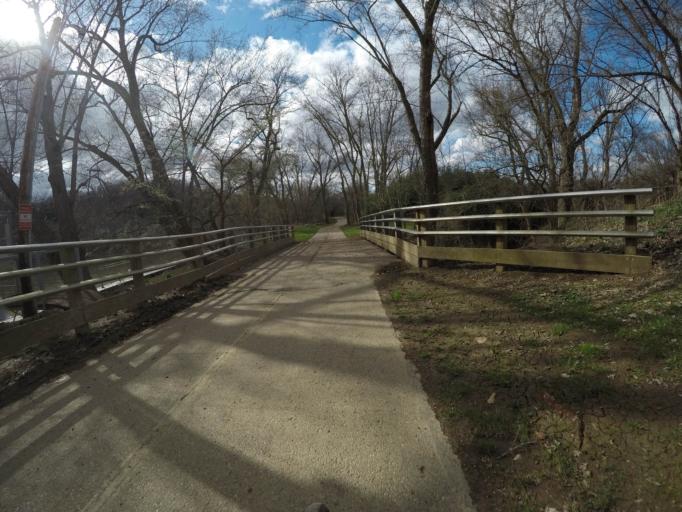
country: US
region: Ohio
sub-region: Washington County
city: Marietta
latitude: 39.4236
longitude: -81.4689
